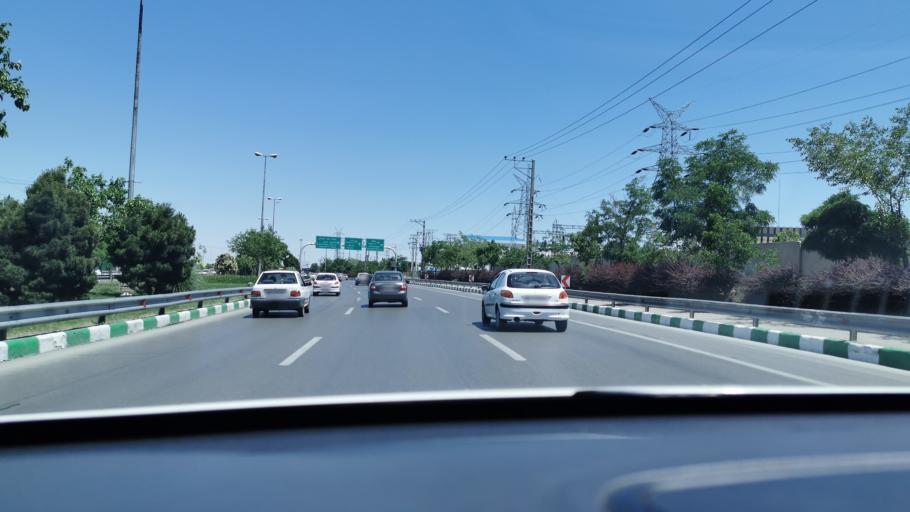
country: IR
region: Razavi Khorasan
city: Mashhad
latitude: 36.2571
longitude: 59.5906
